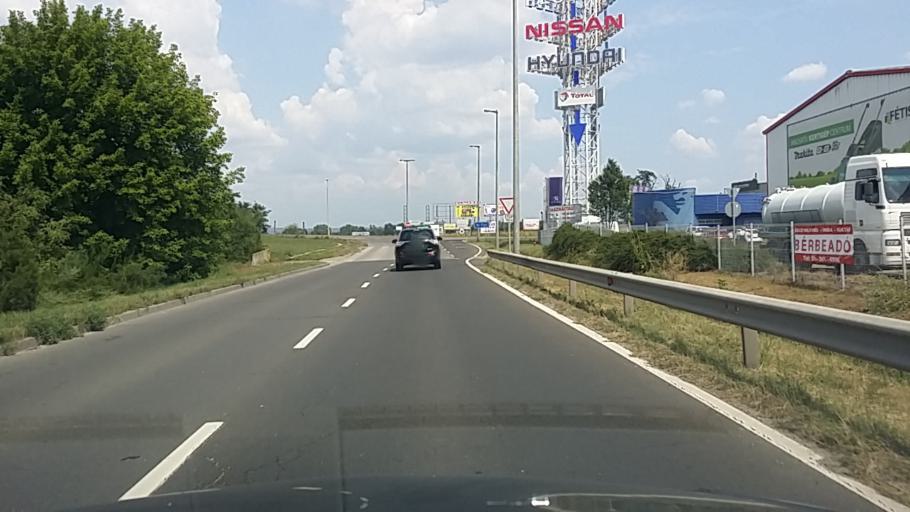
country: HU
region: Budapest
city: Budapest XV. keruelet
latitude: 47.5669
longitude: 19.1496
